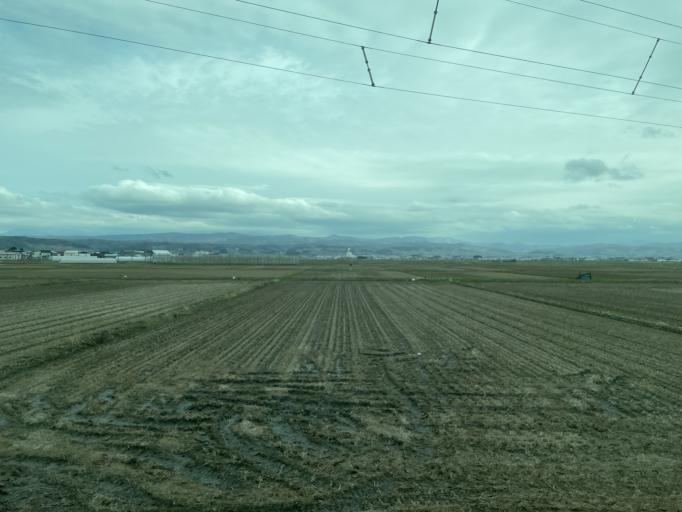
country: JP
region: Aomori
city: Namioka
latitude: 40.7027
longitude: 140.5738
